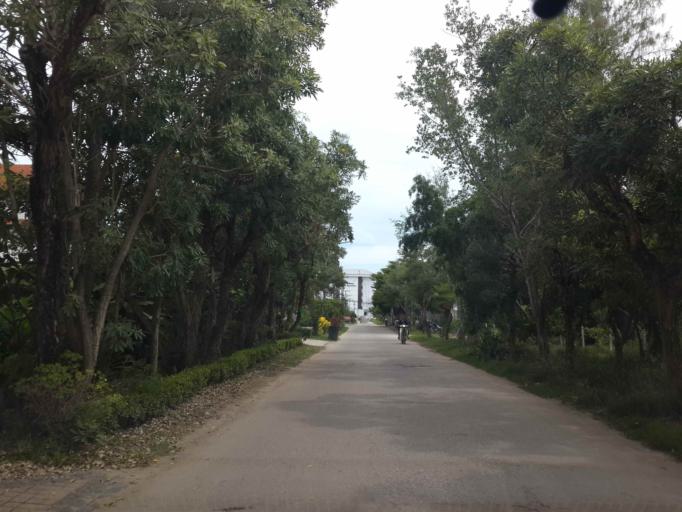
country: TH
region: Prachuap Khiri Khan
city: Hua Hin
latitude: 12.5336
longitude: 99.9679
